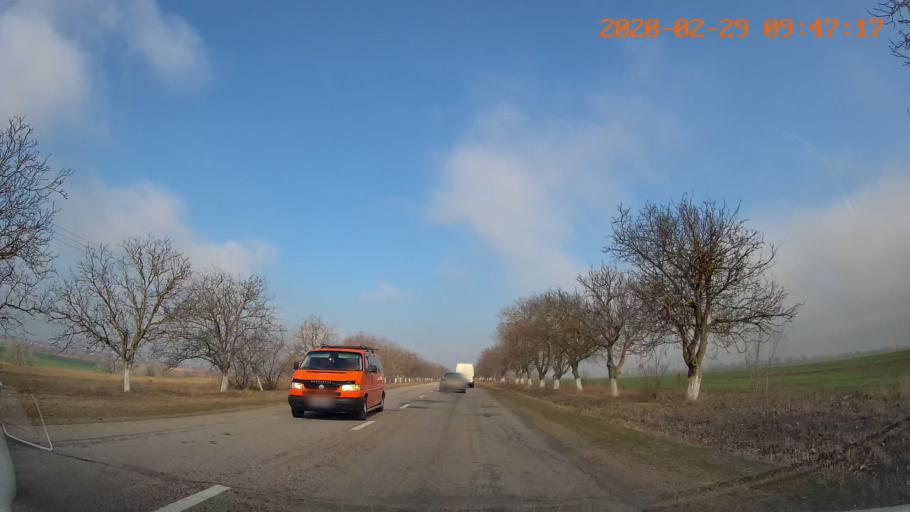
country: MD
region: Telenesti
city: Crasnoe
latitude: 46.6758
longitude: 29.7917
